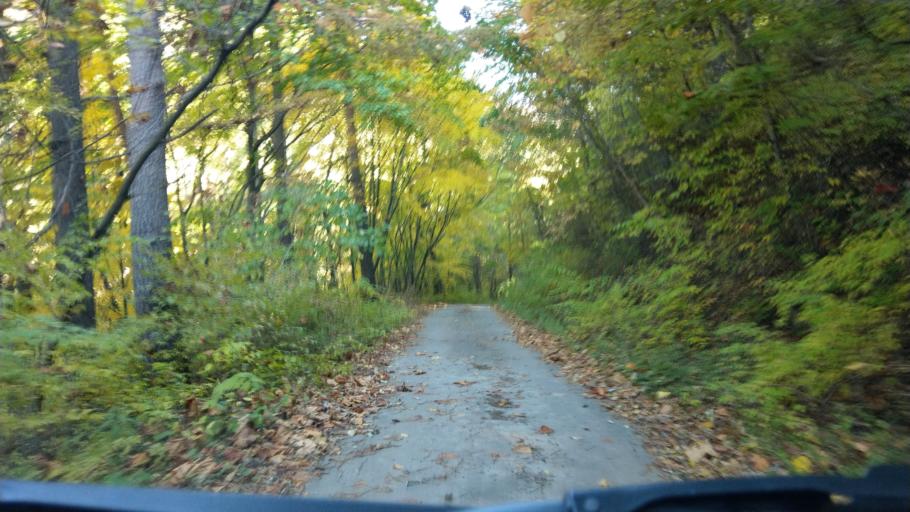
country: JP
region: Nagano
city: Komoro
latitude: 36.3772
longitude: 138.4305
